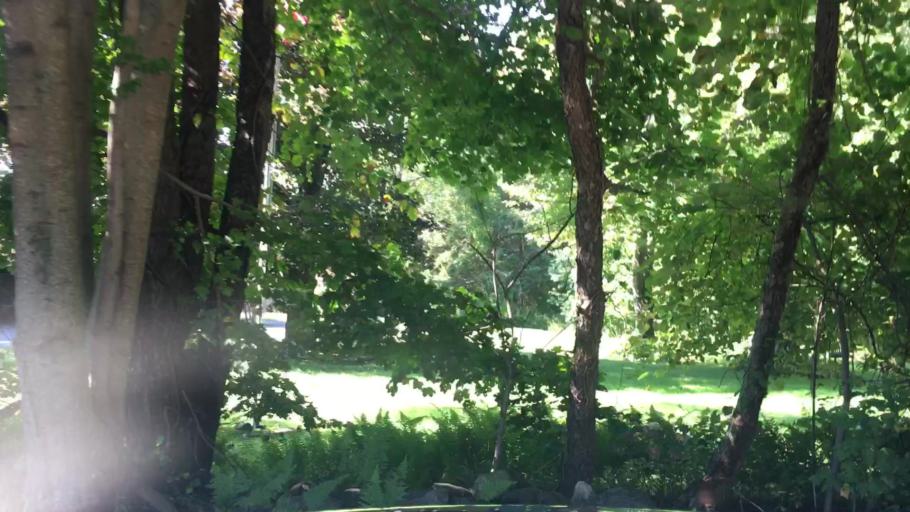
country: US
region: Connecticut
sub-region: Tolland County
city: Rockville
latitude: 41.8691
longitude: -72.4120
